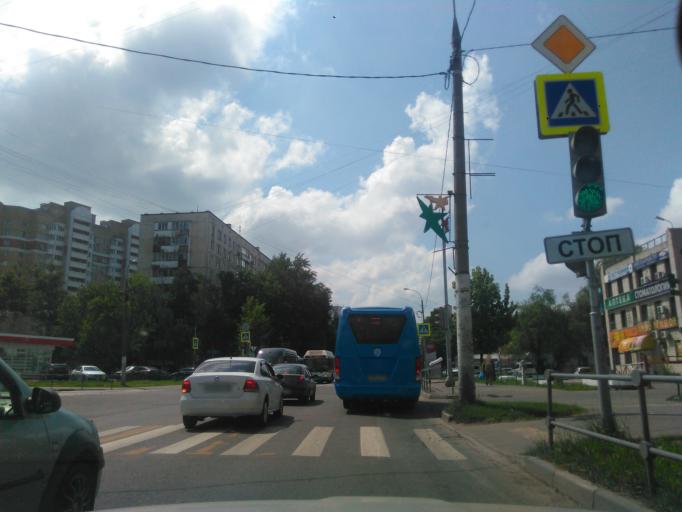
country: RU
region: Moscow
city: Zapadnoye Degunino
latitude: 55.8874
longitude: 37.5244
